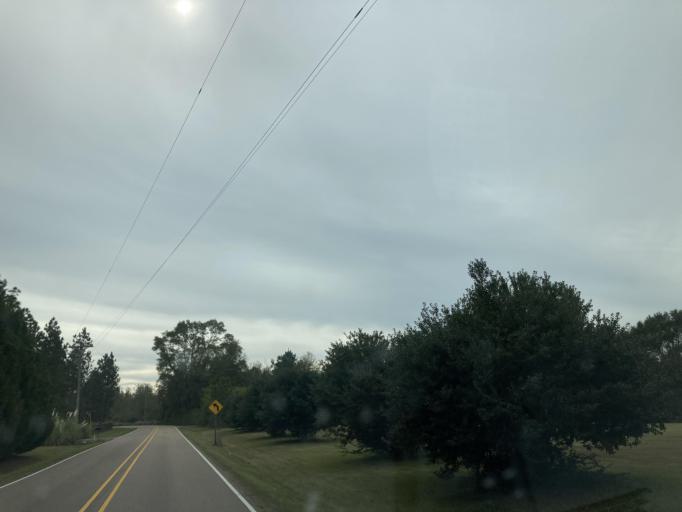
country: US
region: Mississippi
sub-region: Lamar County
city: Lumberton
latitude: 31.0612
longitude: -89.4801
